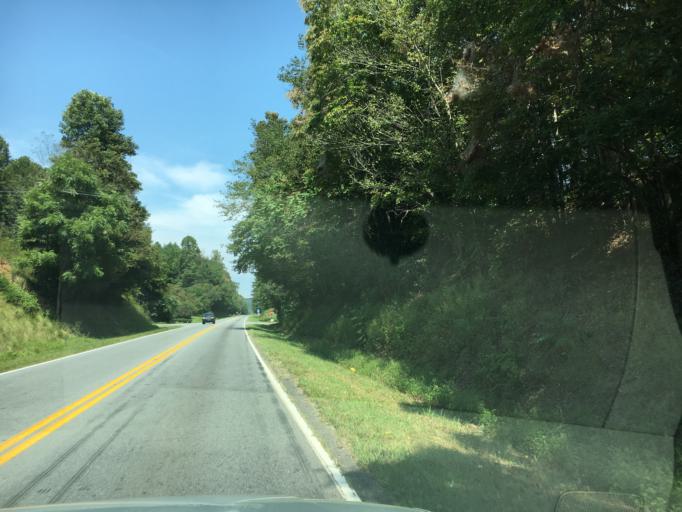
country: US
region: North Carolina
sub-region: McDowell County
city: West Marion
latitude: 35.6266
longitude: -81.9865
